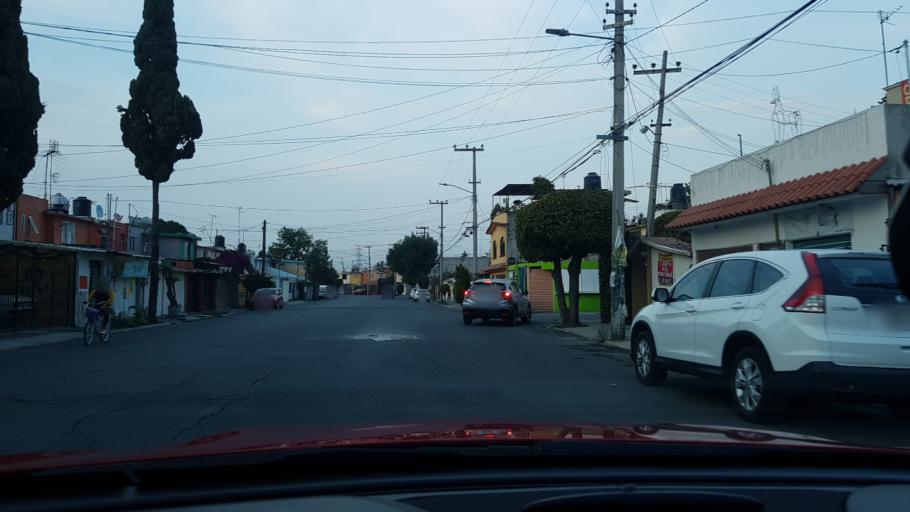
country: MX
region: Mexico
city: Cuautitlan
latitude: 19.6879
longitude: -99.2063
